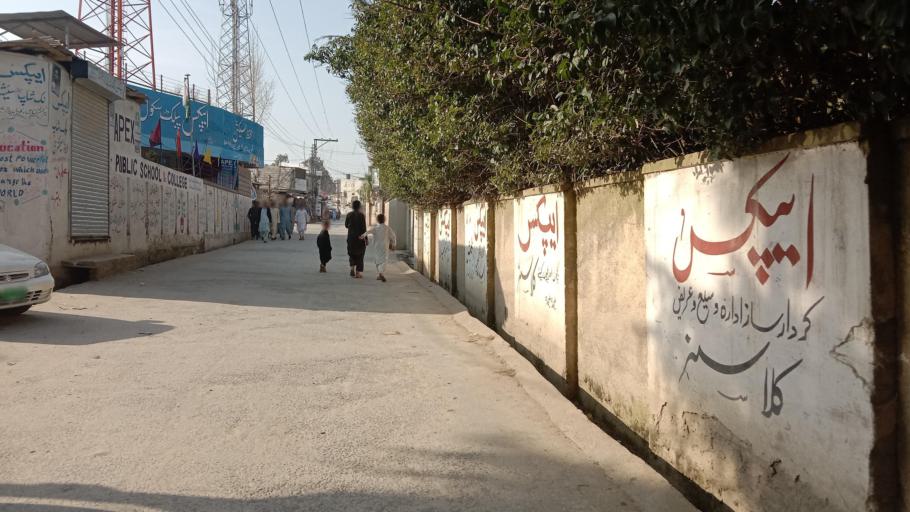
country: PK
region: Khyber Pakhtunkhwa
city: Abbottabad
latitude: 34.1997
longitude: 73.2276
